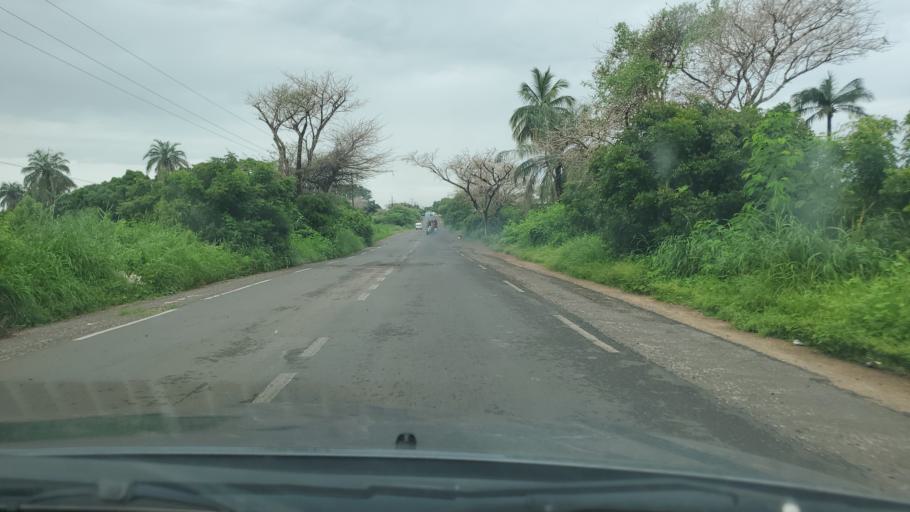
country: SN
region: Thies
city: Mekhe
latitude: 15.1246
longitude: -16.8658
